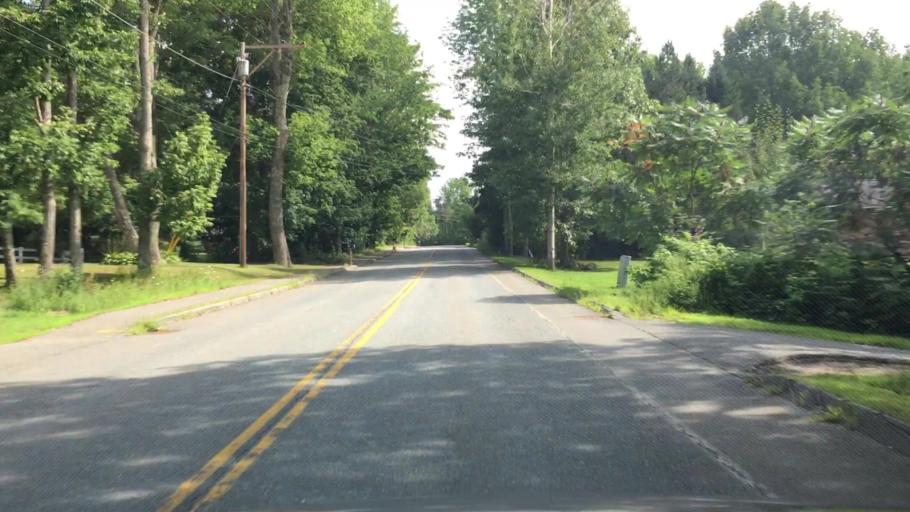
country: US
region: Maine
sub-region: Penobscot County
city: Hampden
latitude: 44.7337
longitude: -68.8593
